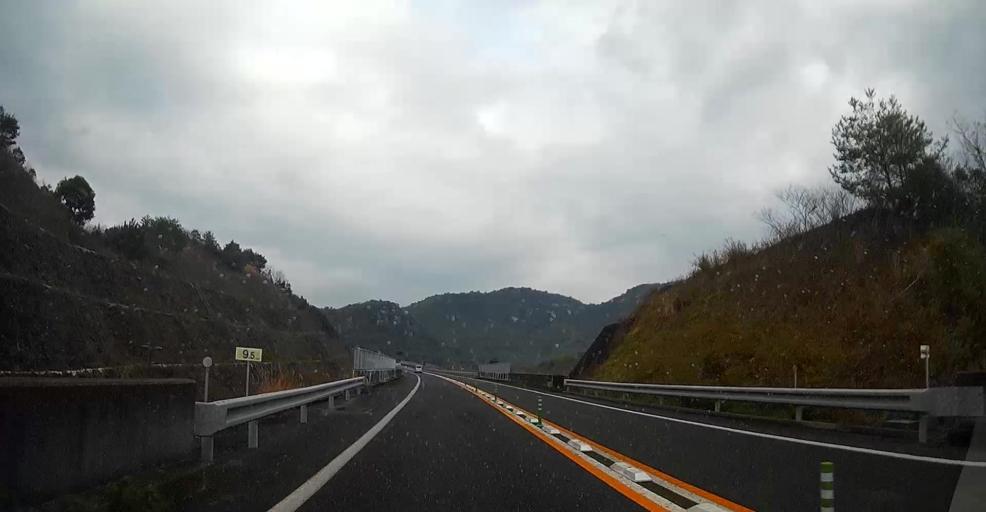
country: JP
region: Kumamoto
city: Yatsushiro
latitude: 32.4998
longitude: 130.3980
